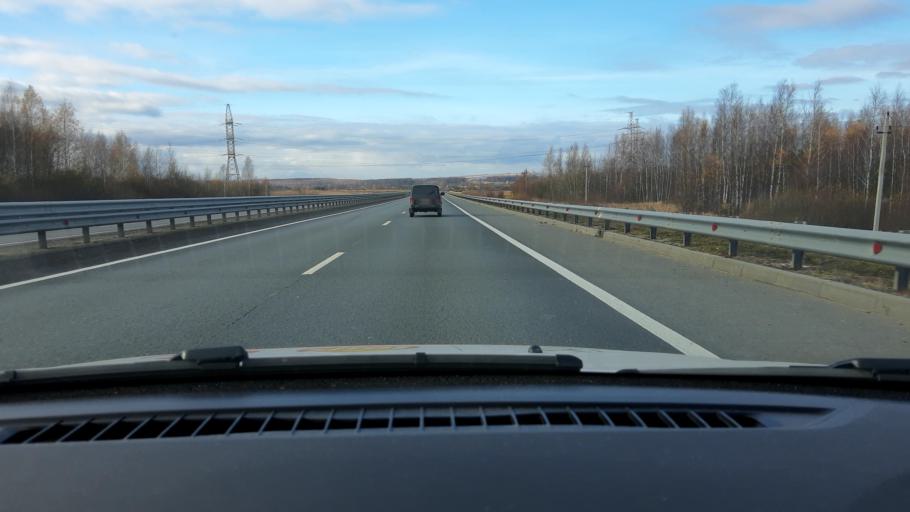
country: RU
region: Nizjnij Novgorod
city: Burevestnik
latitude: 56.1141
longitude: 43.8849
